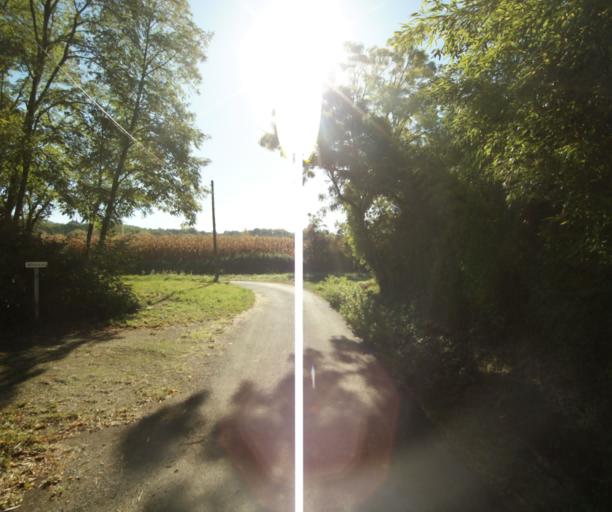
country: FR
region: Midi-Pyrenees
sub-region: Departement du Gers
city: Gondrin
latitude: 43.8381
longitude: 0.2457
